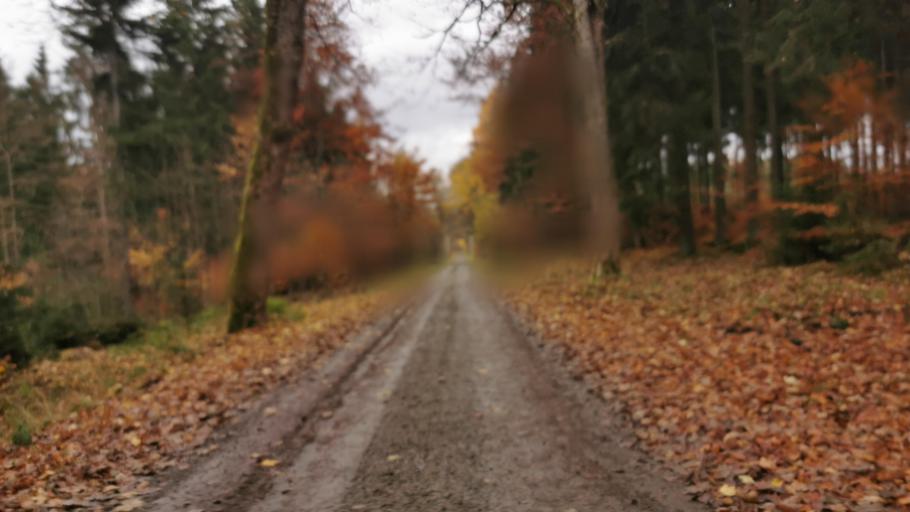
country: DE
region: Thuringia
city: Wurzbach
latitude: 50.4237
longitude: 11.5407
